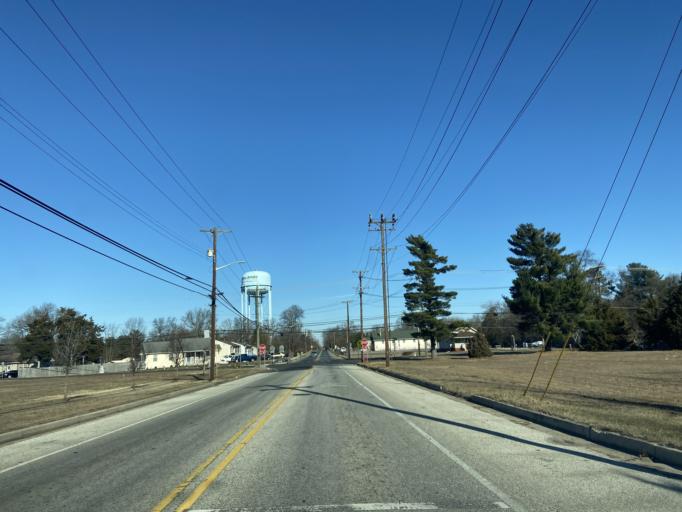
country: US
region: New Jersey
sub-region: Cumberland County
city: Vineland
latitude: 39.4943
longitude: -75.0609
